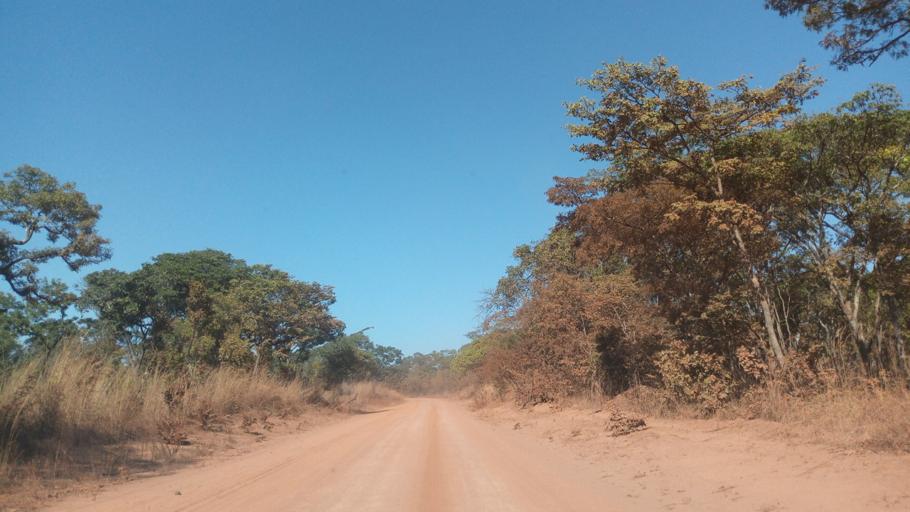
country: ZM
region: Luapula
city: Mwense
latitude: -10.7150
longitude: 28.3635
